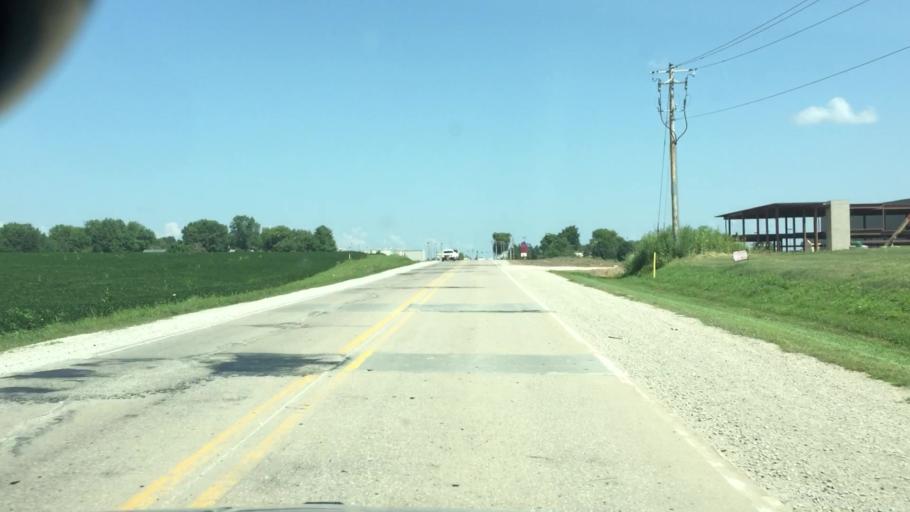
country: US
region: Iowa
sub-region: Jasper County
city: Newton
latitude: 41.6931
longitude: -93.0144
